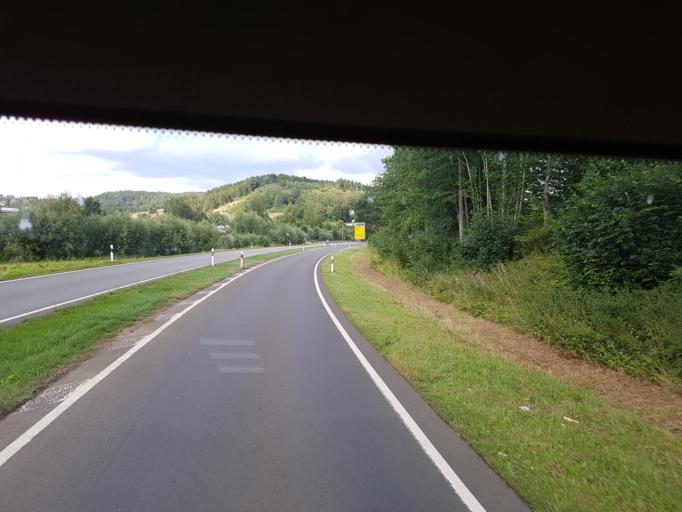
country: DE
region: Rheinland-Pfalz
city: Rockeskyll
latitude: 50.2462
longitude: 6.6936
